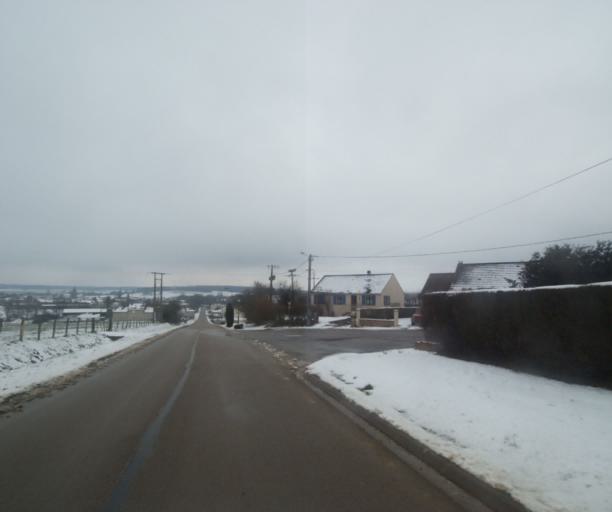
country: FR
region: Champagne-Ardenne
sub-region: Departement de la Haute-Marne
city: Laneuville-a-Remy
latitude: 48.4203
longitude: 4.8379
